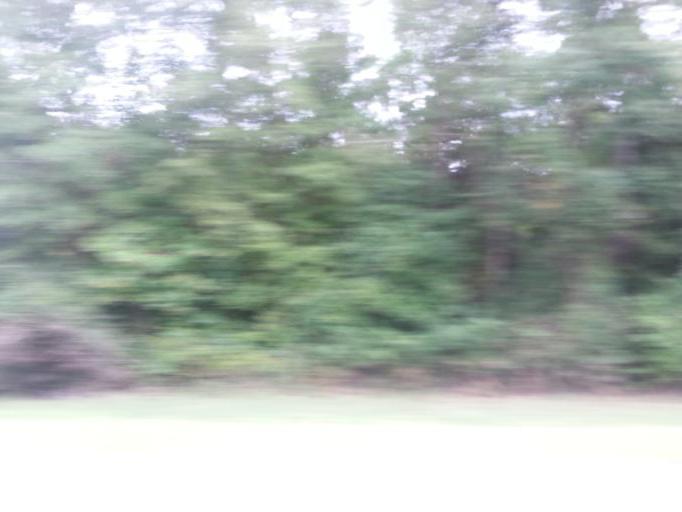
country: US
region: Alabama
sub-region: Conecuh County
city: Evergreen
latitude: 31.3718
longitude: -87.0507
